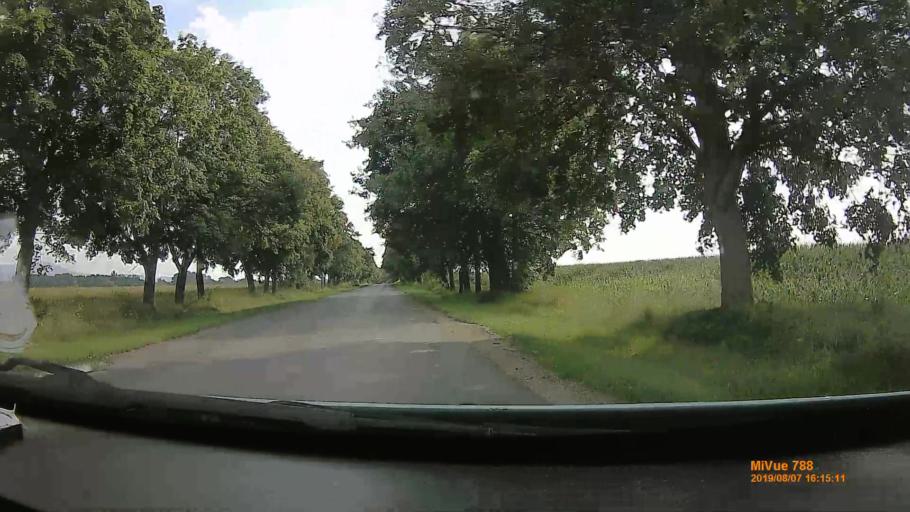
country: HU
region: Borsod-Abauj-Zemplen
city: Gonc
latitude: 48.4712
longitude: 21.2562
